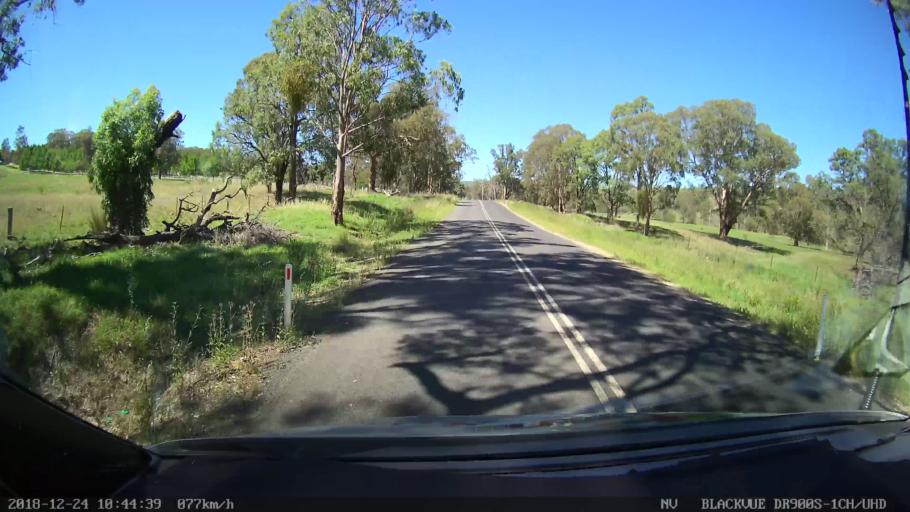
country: AU
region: New South Wales
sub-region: Upper Hunter Shire
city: Merriwa
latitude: -31.8951
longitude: 150.4423
